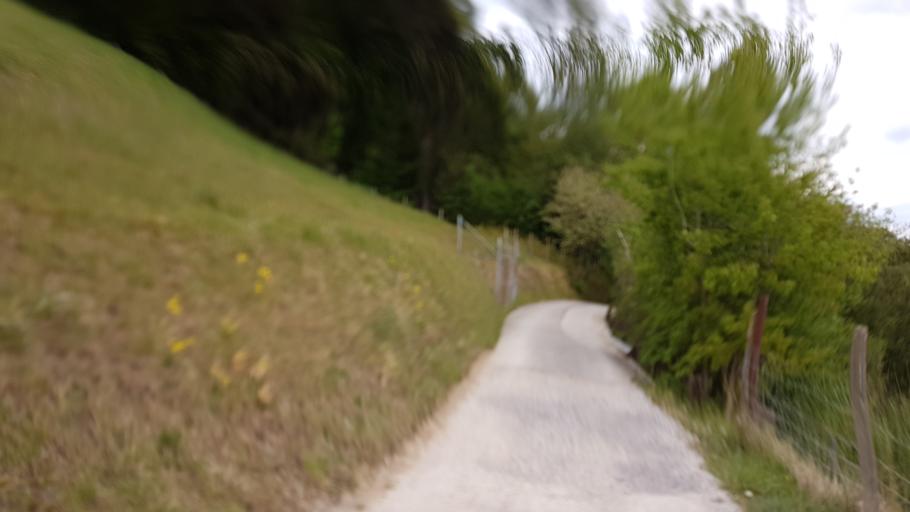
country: CH
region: Bern
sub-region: Bern-Mittelland District
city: Munsingen
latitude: 46.8611
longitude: 7.5489
